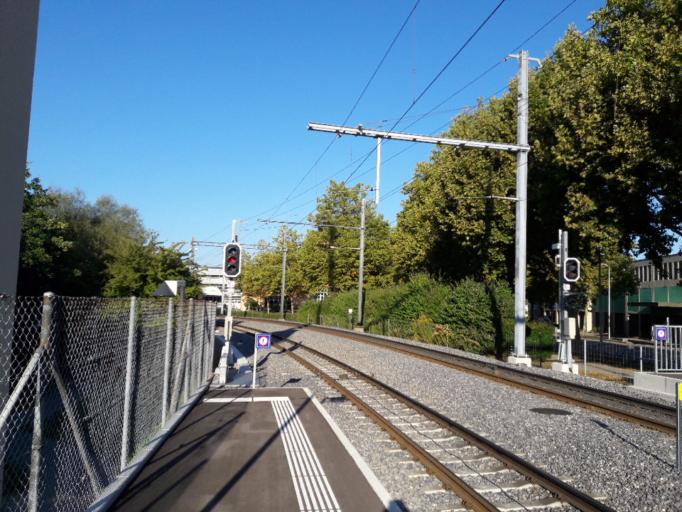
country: CH
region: Bern
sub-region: Bern-Mittelland District
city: Bolligen
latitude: 46.9734
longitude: 7.4831
